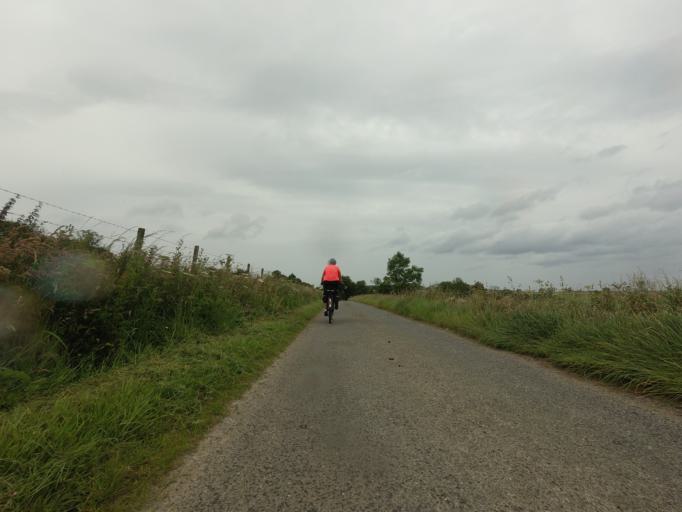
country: GB
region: Scotland
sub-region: Moray
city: Cullen
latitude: 57.6698
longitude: -2.7697
